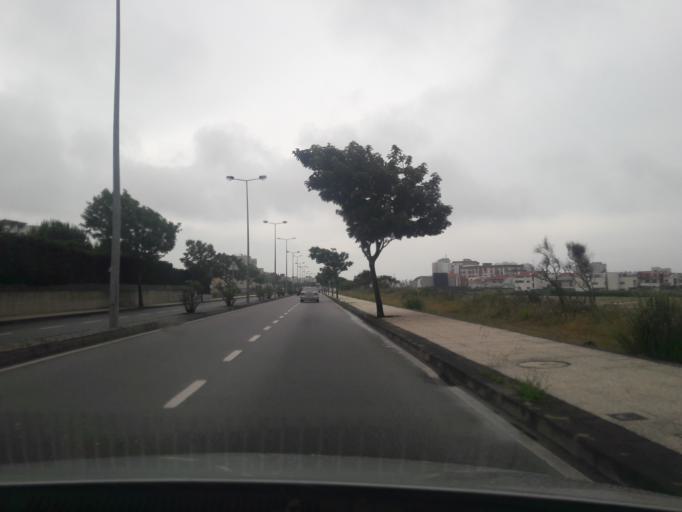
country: PT
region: Porto
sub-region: Povoa de Varzim
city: Povoa de Varzim
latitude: 41.3932
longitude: -8.7582
